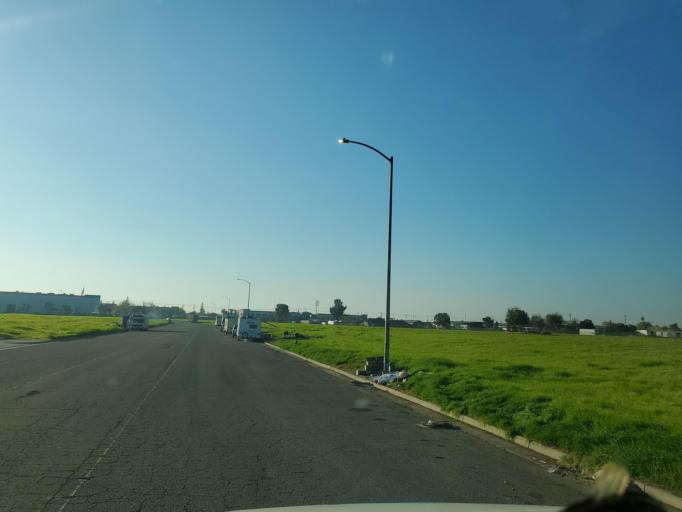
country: US
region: California
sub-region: San Joaquin County
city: Kennedy
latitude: 37.9094
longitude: -121.2196
